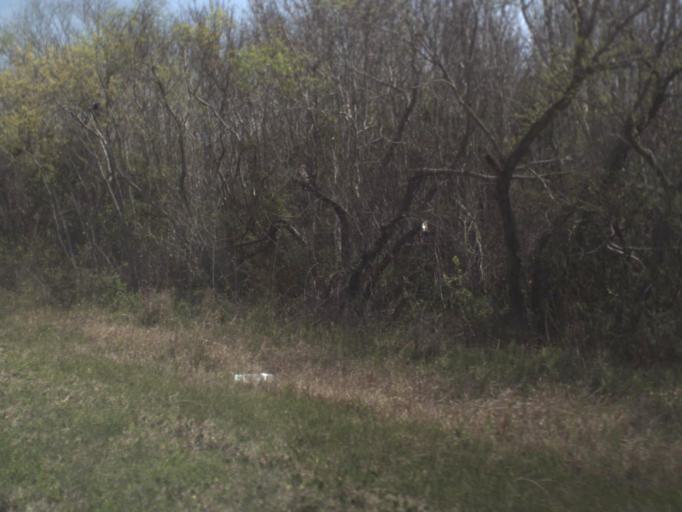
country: US
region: Florida
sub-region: Gulf County
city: Port Saint Joe
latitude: 29.6743
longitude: -85.3482
